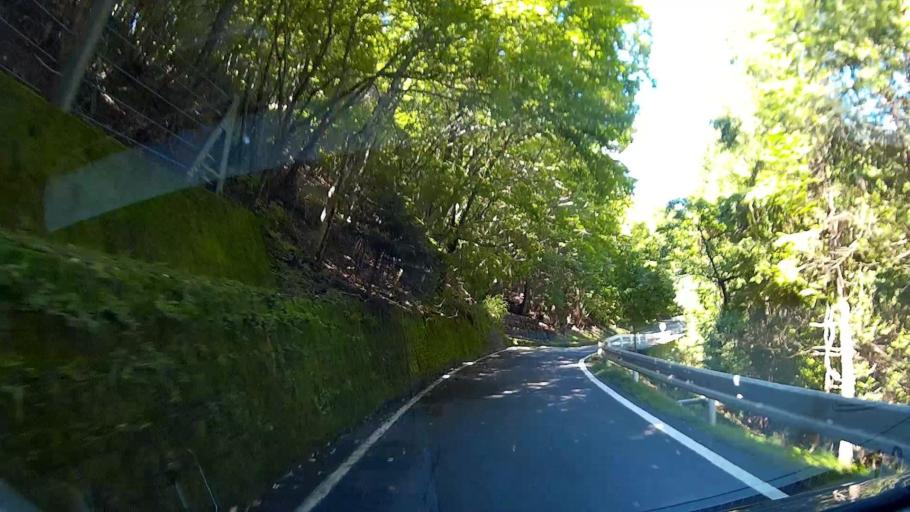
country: JP
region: Shizuoka
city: Shizuoka-shi
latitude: 35.1979
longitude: 138.2599
